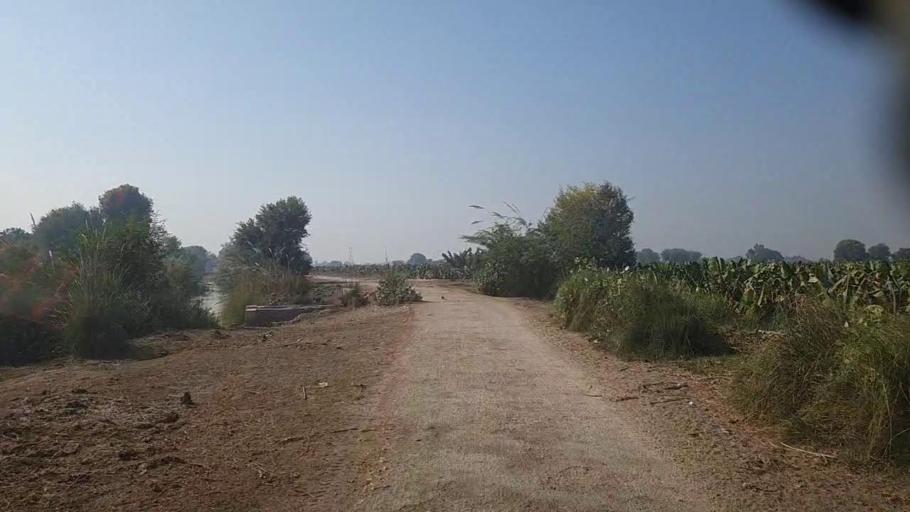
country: PK
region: Sindh
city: Kandiari
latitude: 27.0090
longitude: 68.4979
